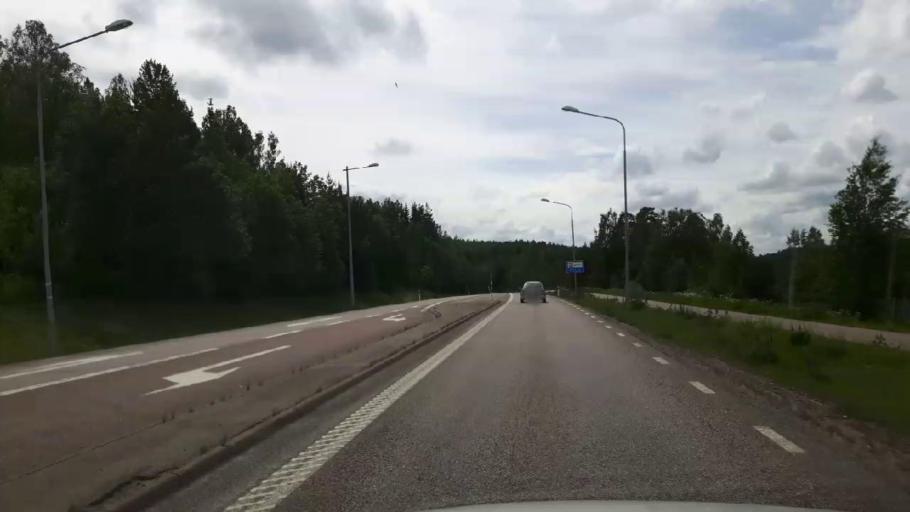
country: SE
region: Vaestmanland
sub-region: Fagersta Kommun
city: Fagersta
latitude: 59.9792
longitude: 15.7946
